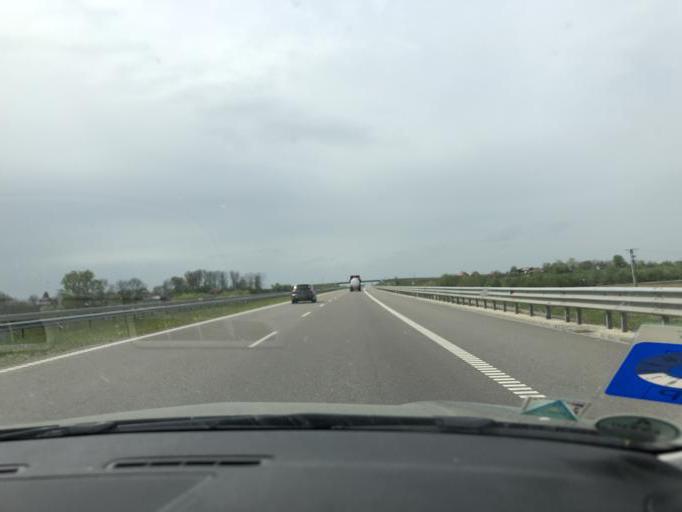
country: PL
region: Subcarpathian Voivodeship
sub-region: Powiat jaroslawski
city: Sosnica
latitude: 49.9179
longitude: 22.8714
